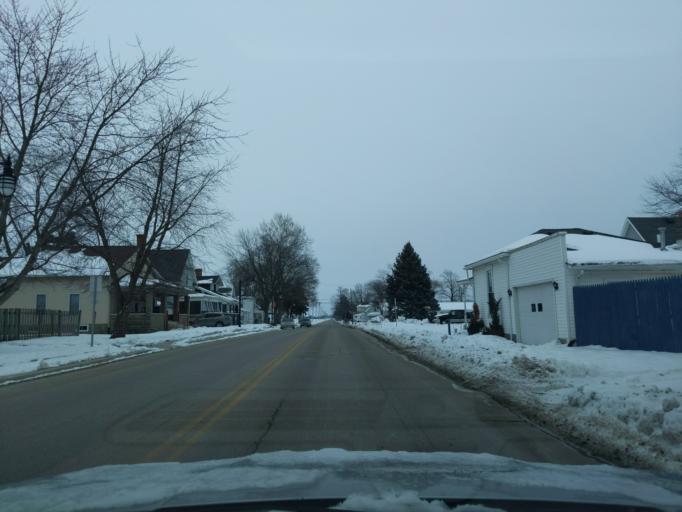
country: US
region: Indiana
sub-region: Benton County
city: Otterbein
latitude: 40.4904
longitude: -87.0957
